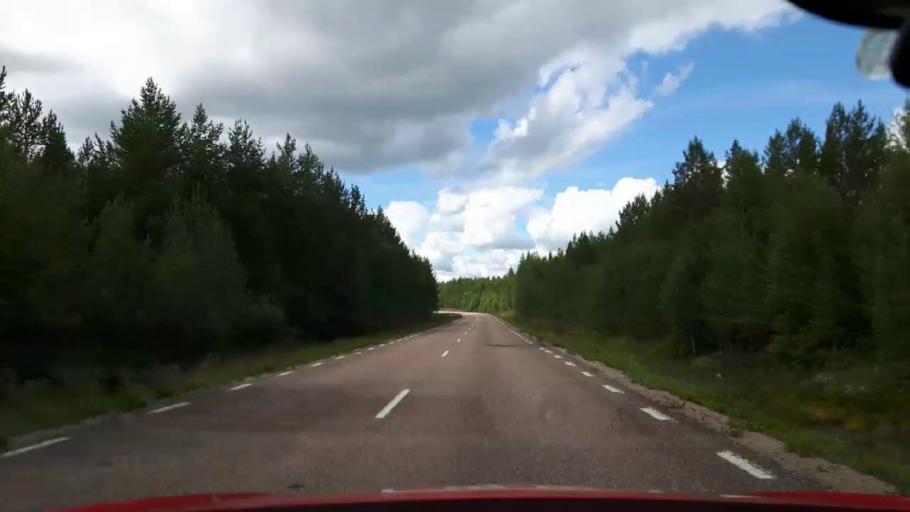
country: SE
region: Jaemtland
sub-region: Harjedalens Kommun
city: Sveg
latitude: 61.8332
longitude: 13.9035
